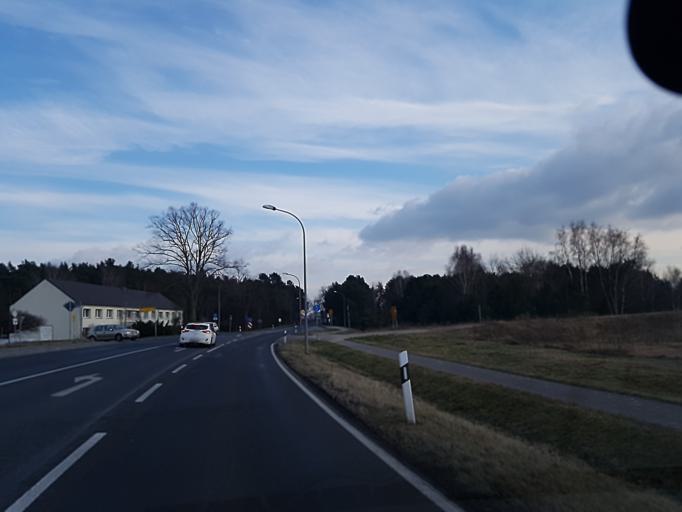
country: DE
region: Brandenburg
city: Belzig
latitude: 52.1310
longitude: 12.6288
